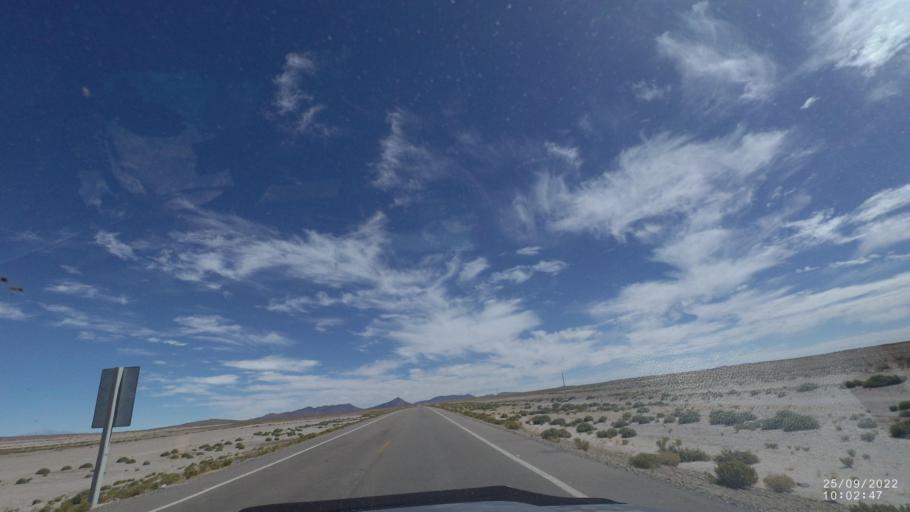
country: BO
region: Potosi
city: Colchani
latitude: -20.2305
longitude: -66.9535
